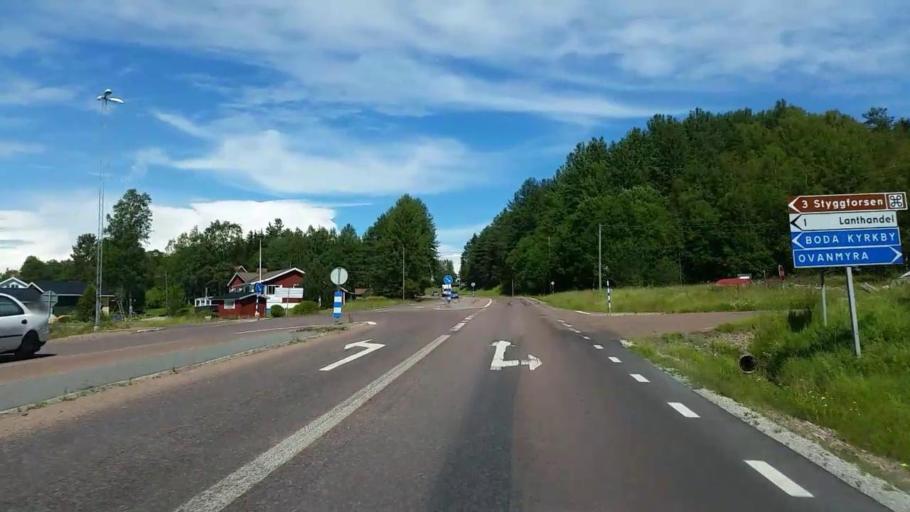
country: SE
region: Dalarna
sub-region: Rattviks Kommun
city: Raettvik
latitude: 61.0041
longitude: 15.2190
